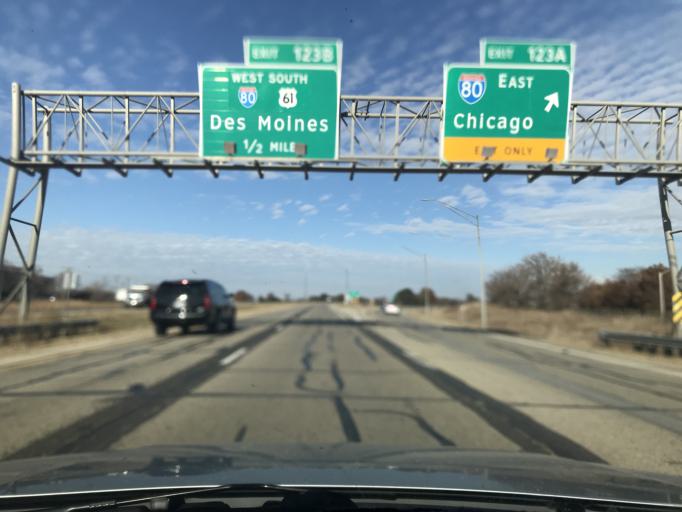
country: US
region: Iowa
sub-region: Scott County
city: Davenport
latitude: 41.5900
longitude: -90.5710
